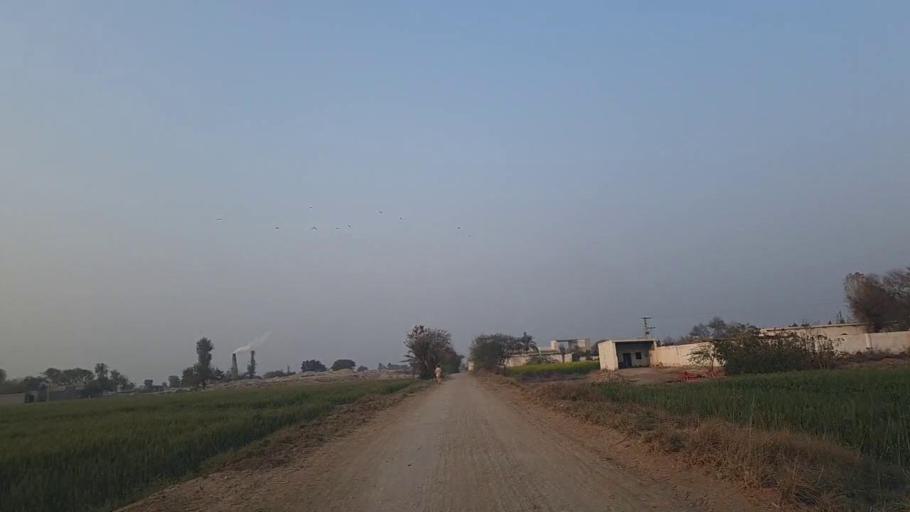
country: PK
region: Sindh
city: Nawabshah
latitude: 26.2795
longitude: 68.4648
